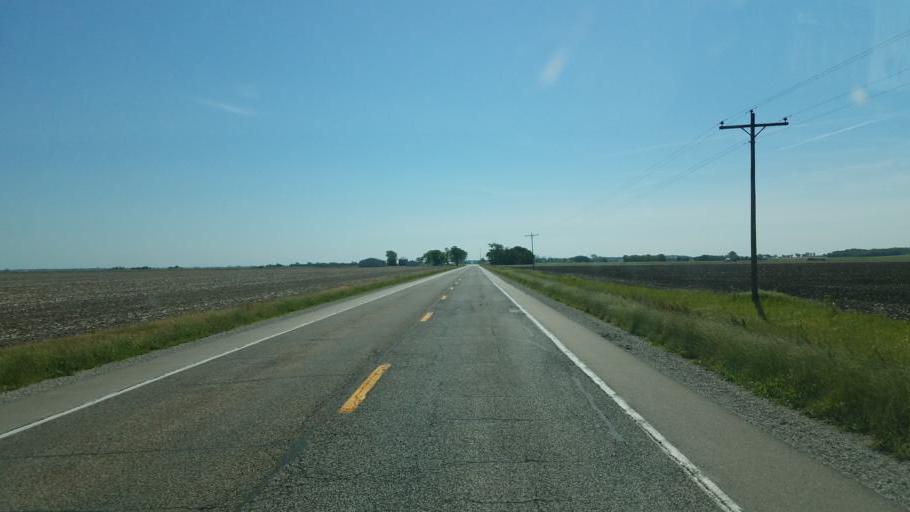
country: US
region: Illinois
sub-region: Mason County
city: Mason City
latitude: 40.3047
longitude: -89.7061
